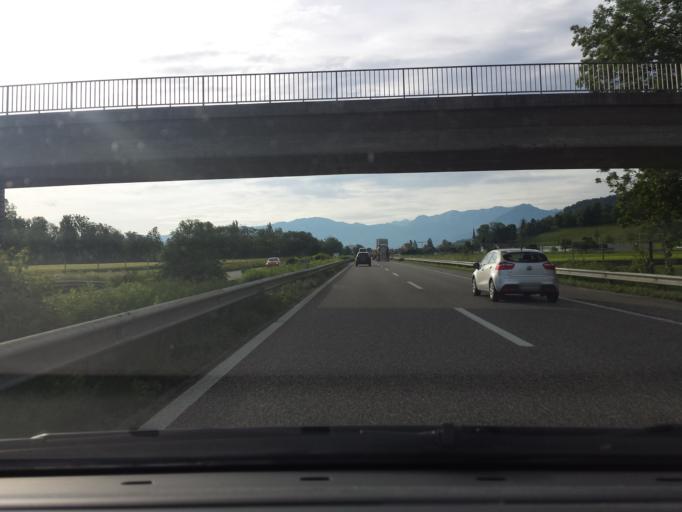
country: CH
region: Appenzell Ausserrhoden
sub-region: Bezirk Vorderland
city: Walzenhausen
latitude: 47.4599
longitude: 9.6141
